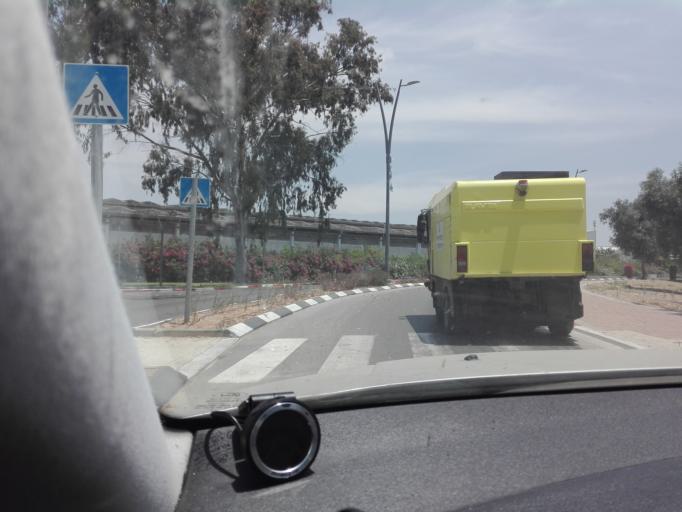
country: IL
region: Central District
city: Bene 'Ayish
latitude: 31.7379
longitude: 34.7485
